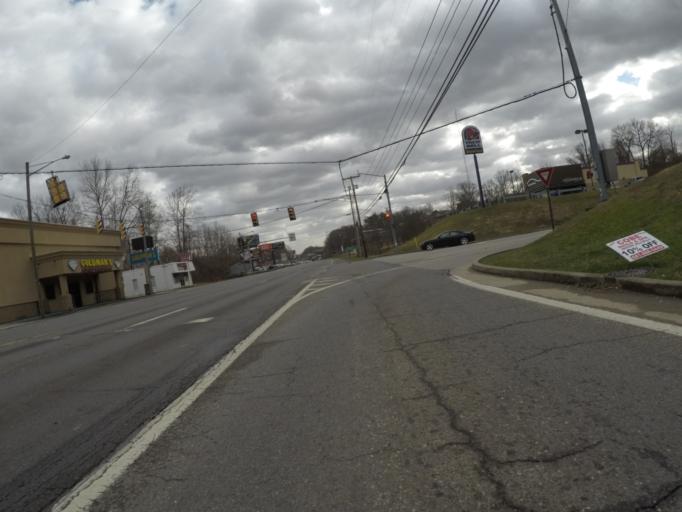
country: US
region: West Virginia
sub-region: Cabell County
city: Pea Ridge
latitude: 38.4107
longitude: -82.3765
